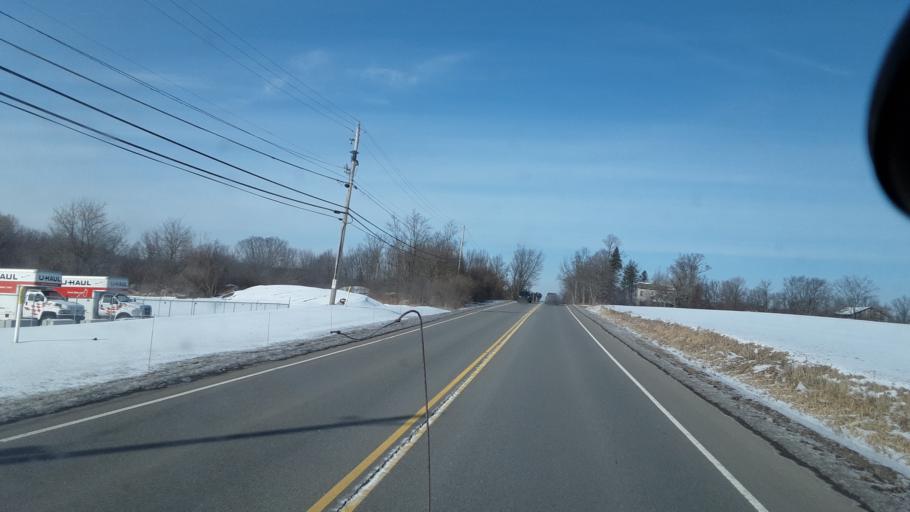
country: US
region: Ohio
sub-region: Mahoning County
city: Canfield
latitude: 40.9935
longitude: -80.7607
